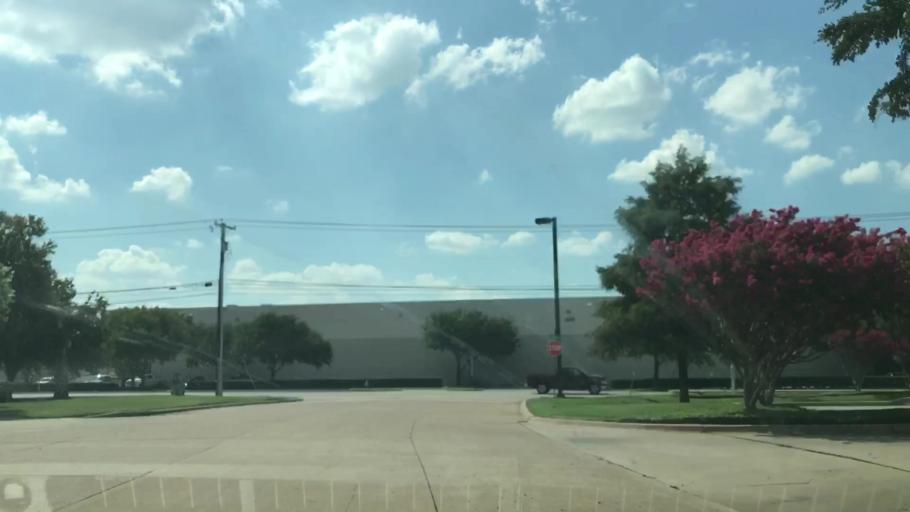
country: US
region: Texas
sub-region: Dallas County
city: Farmers Branch
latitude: 32.9431
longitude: -96.9245
